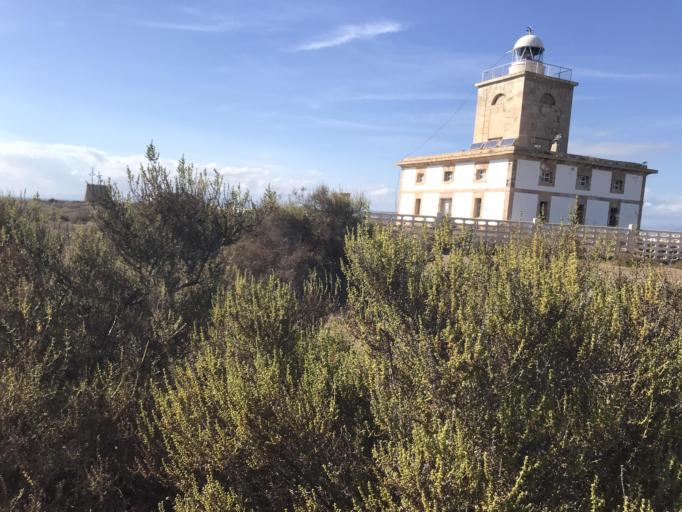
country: ES
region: Valencia
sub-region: Provincia de Alicante
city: Santa Pola
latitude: 38.1638
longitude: -0.4708
